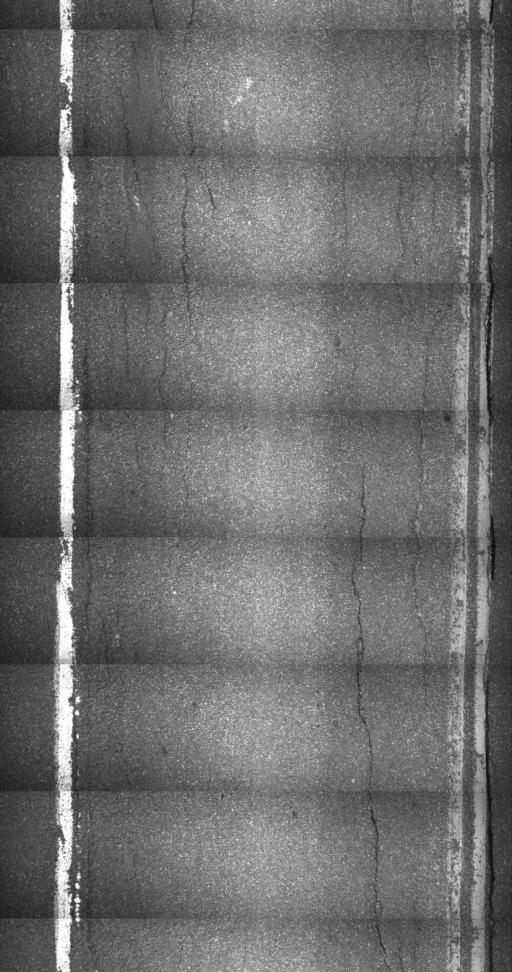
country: US
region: Vermont
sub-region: Chittenden County
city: Hinesburg
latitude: 44.3962
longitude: -73.1278
